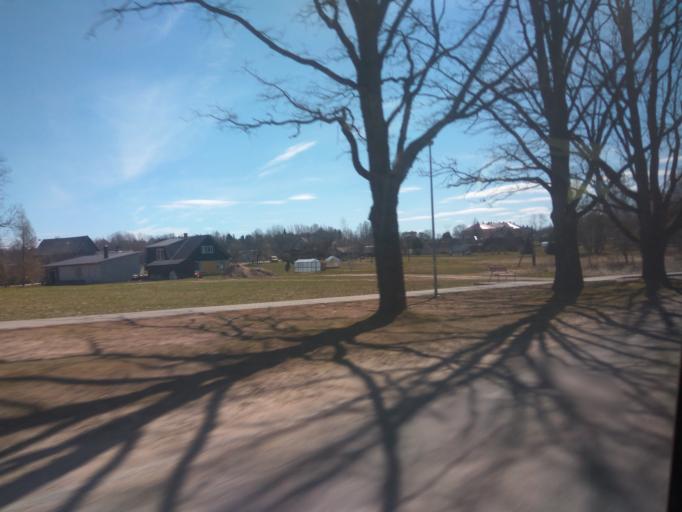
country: LV
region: Aluksnes Rajons
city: Aluksne
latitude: 57.4361
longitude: 27.0384
